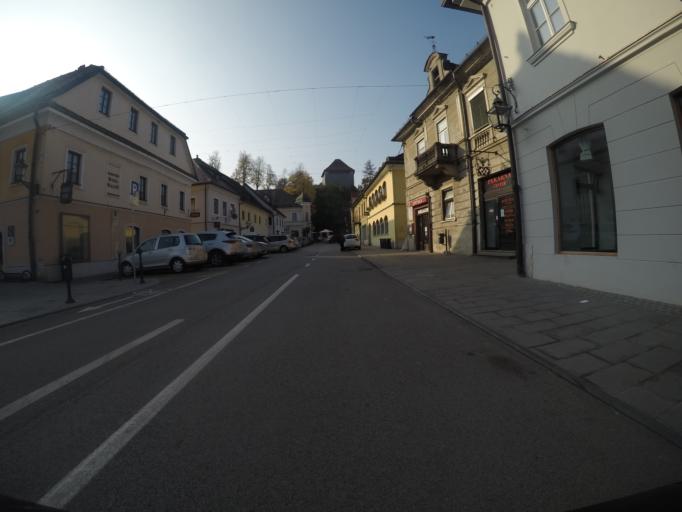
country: SI
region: Kamnik
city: Kamnik
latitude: 46.2256
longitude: 14.6116
